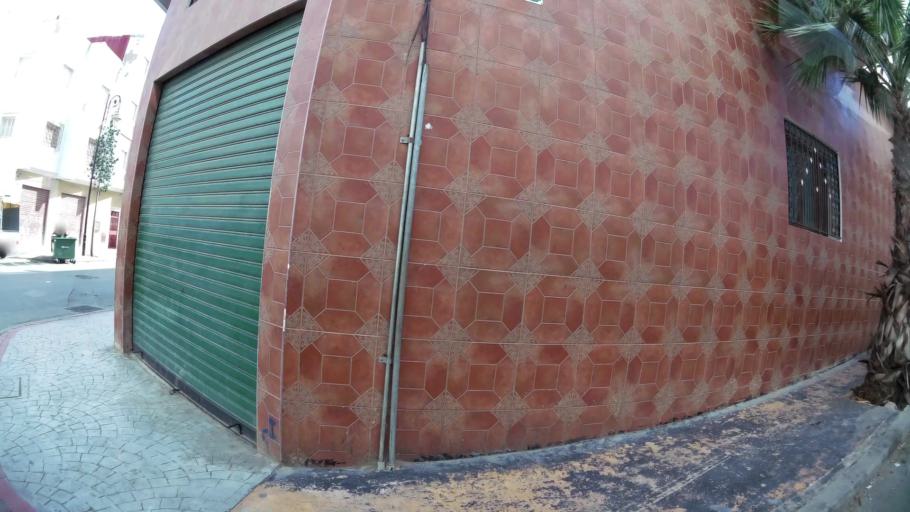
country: MA
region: Tanger-Tetouan
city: Tetouan
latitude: 35.5890
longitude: -5.3553
